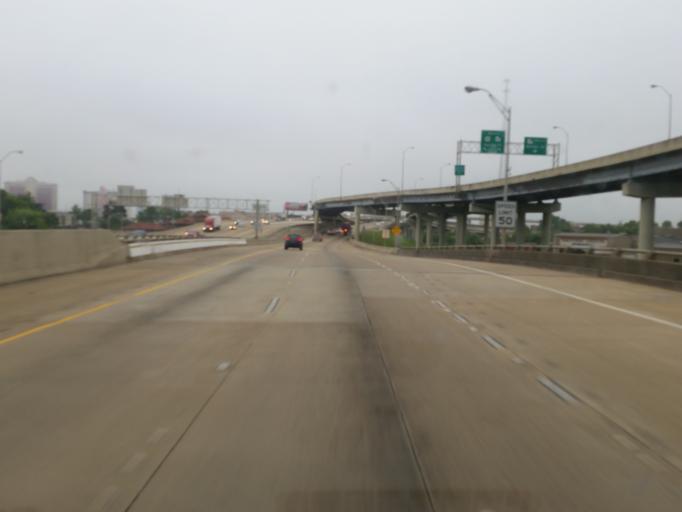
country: US
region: Louisiana
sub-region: Bossier Parish
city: Bossier City
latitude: 32.5057
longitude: -93.7460
